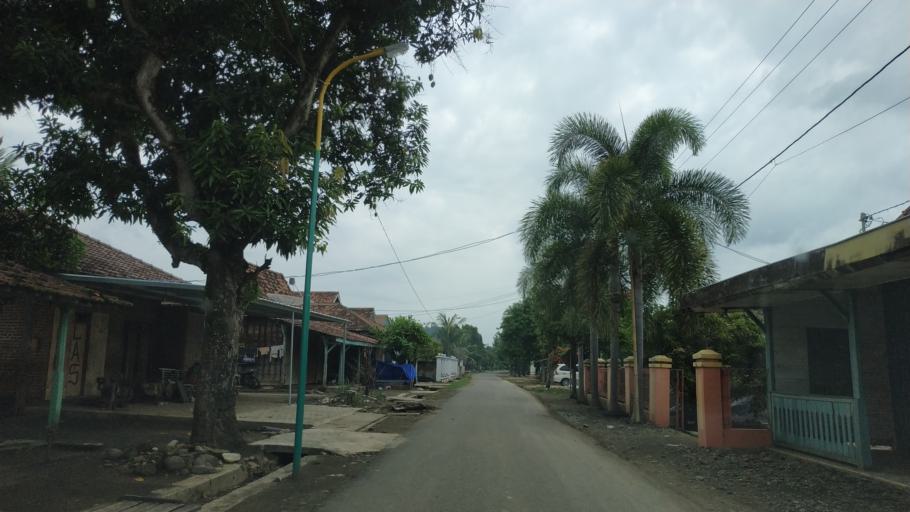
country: ID
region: Central Java
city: Krajan Tegalombo
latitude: -6.4232
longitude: 110.9847
